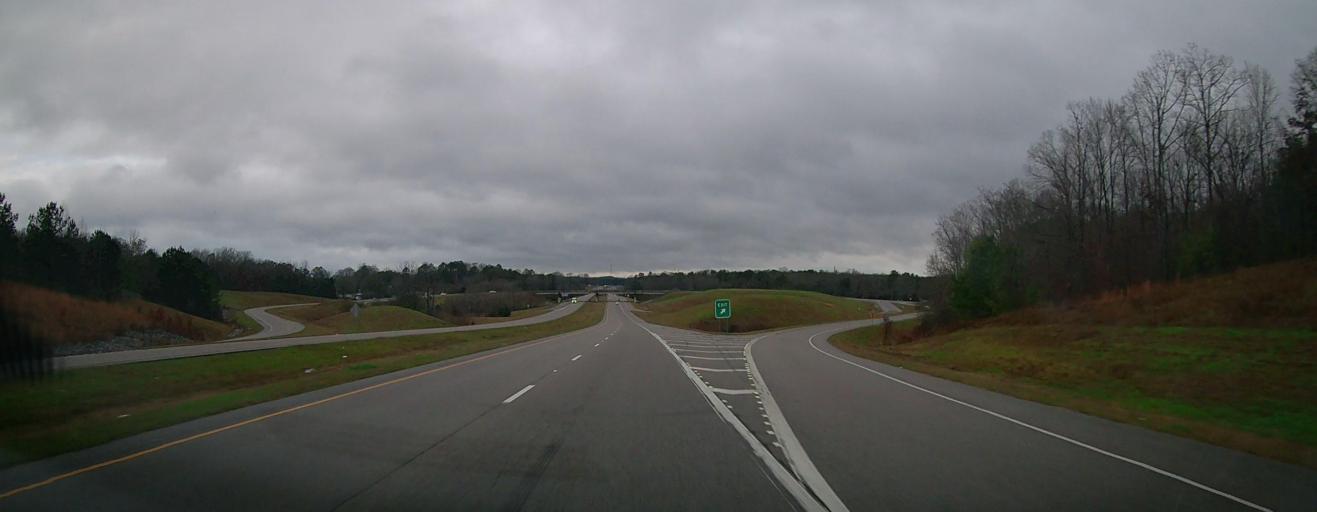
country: US
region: Alabama
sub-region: Bibb County
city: Centreville
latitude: 32.9572
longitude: -87.1296
